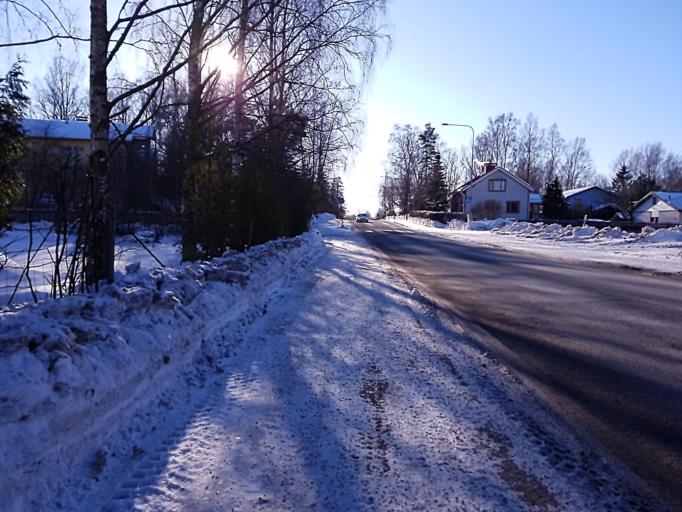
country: FI
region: Uusimaa
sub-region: Helsinki
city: Teekkarikylae
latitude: 60.2464
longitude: 24.8843
